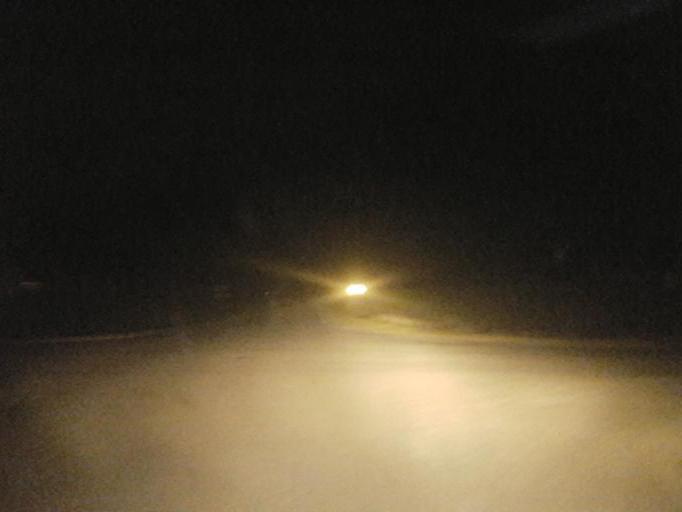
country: US
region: Michigan
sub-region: Montcalm County
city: Edmore
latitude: 43.5238
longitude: -85.0264
